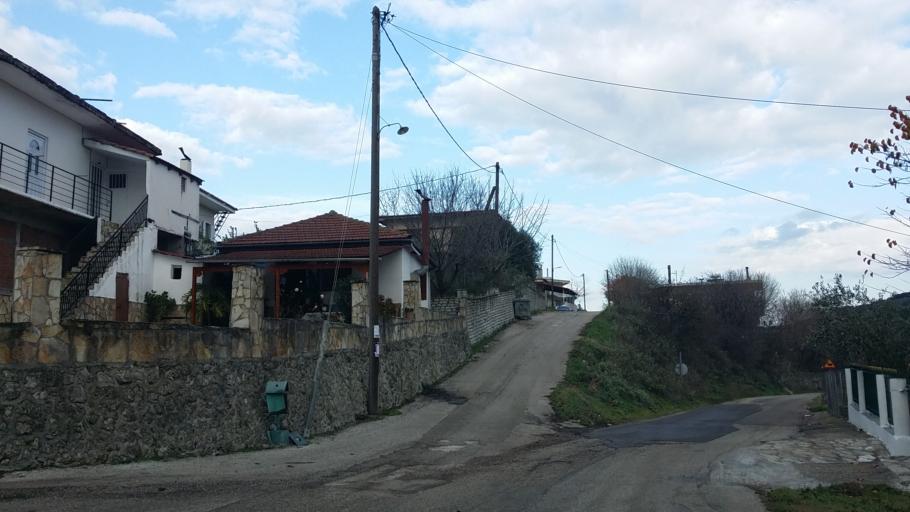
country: GR
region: West Greece
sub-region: Nomos Aitolias kai Akarnanias
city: Katouna
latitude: 38.7868
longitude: 21.1089
